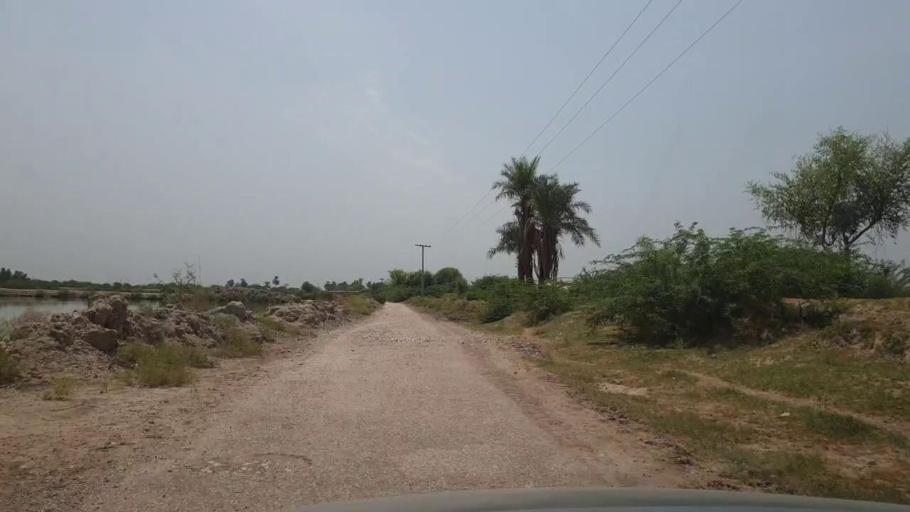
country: PK
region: Sindh
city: Garhi Yasin
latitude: 27.8828
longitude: 68.4954
